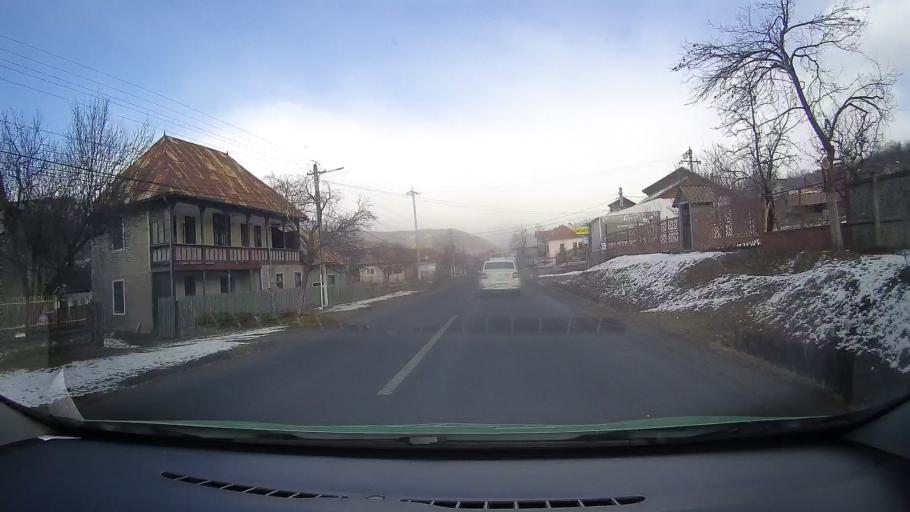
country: RO
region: Dambovita
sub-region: Comuna Moroeni
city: Lunca
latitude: 45.2016
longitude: 25.4416
